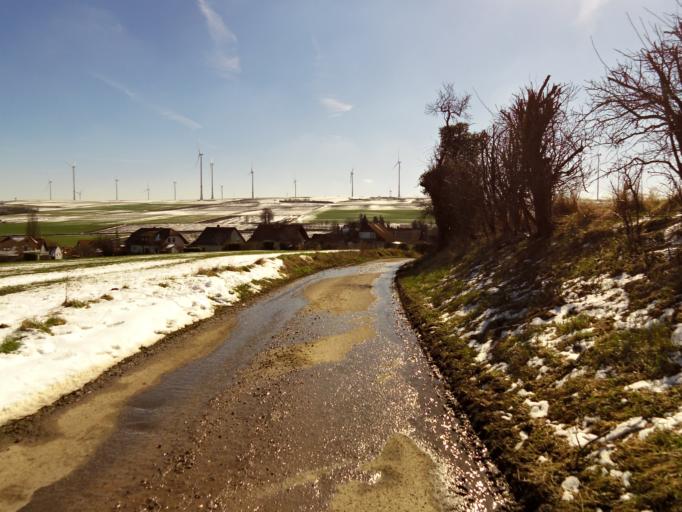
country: DE
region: Rheinland-Pfalz
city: Bubenheim
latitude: 49.6307
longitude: 8.1157
